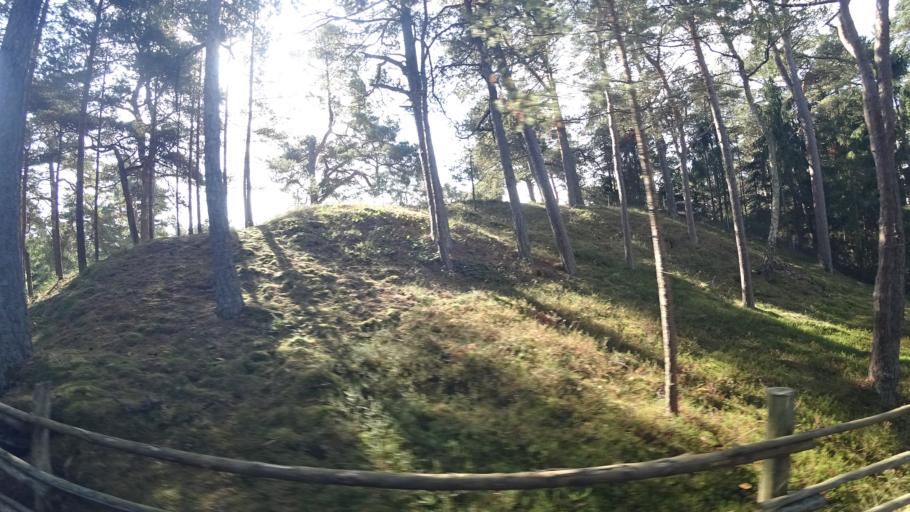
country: SE
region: Skane
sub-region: Kristianstads Kommun
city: Ahus
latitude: 55.9159
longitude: 14.3068
